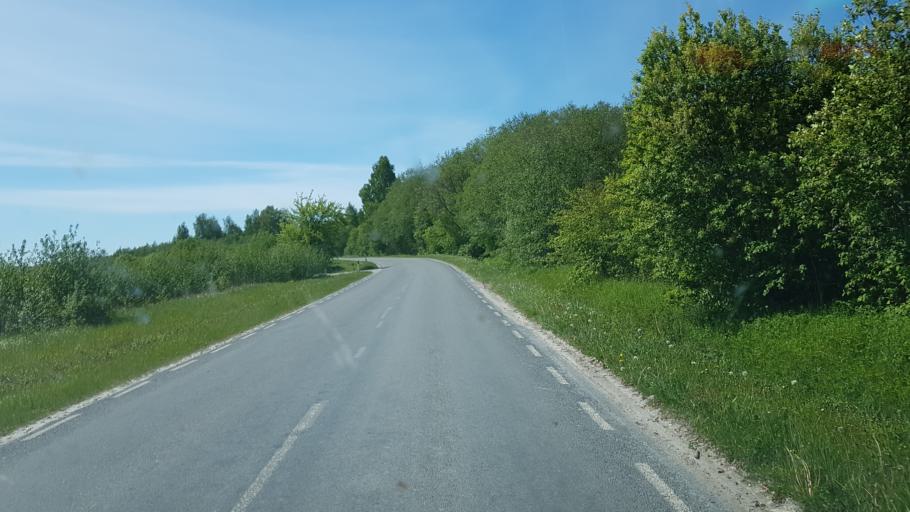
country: EE
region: Saare
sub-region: Kuressaare linn
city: Kuressaare
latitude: 58.2798
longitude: 22.5025
